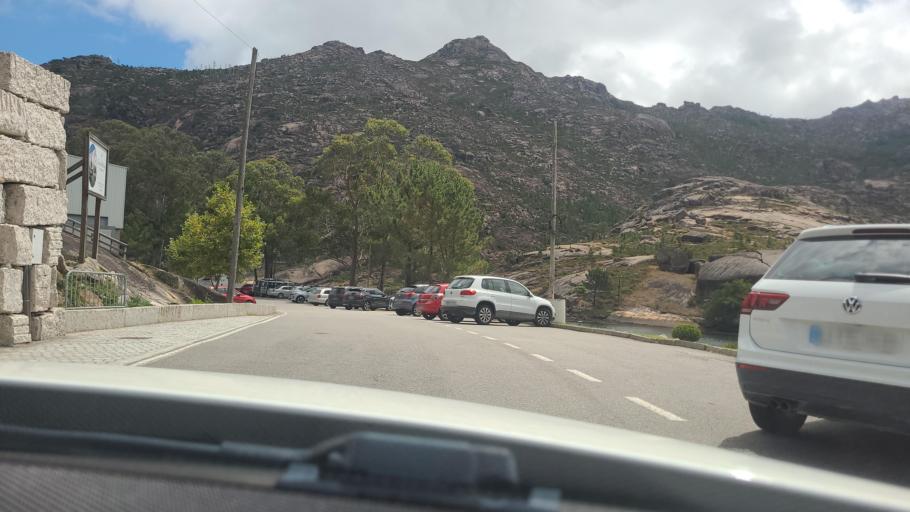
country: ES
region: Galicia
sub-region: Provincia da Coruna
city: Corcubion
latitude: 42.9127
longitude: -9.1235
